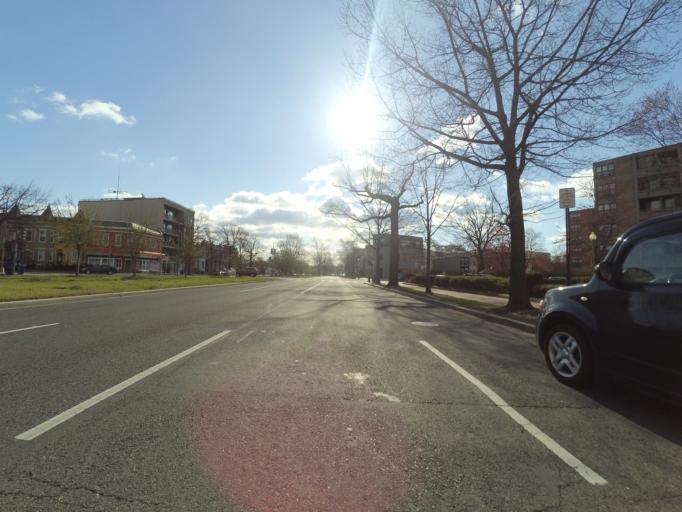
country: US
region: Washington, D.C.
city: Washington, D.C.
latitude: 38.8816
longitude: -76.9890
